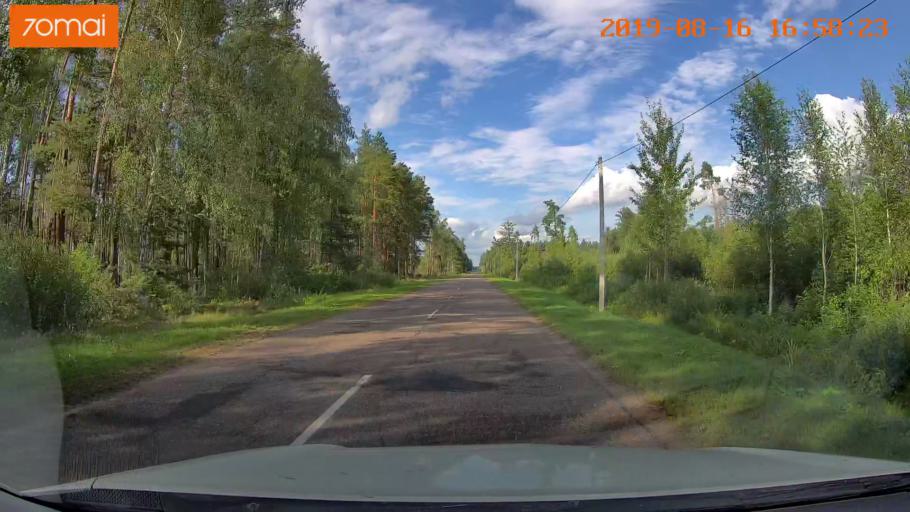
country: BY
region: Mogilev
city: Hlusha
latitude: 53.2686
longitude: 28.8329
